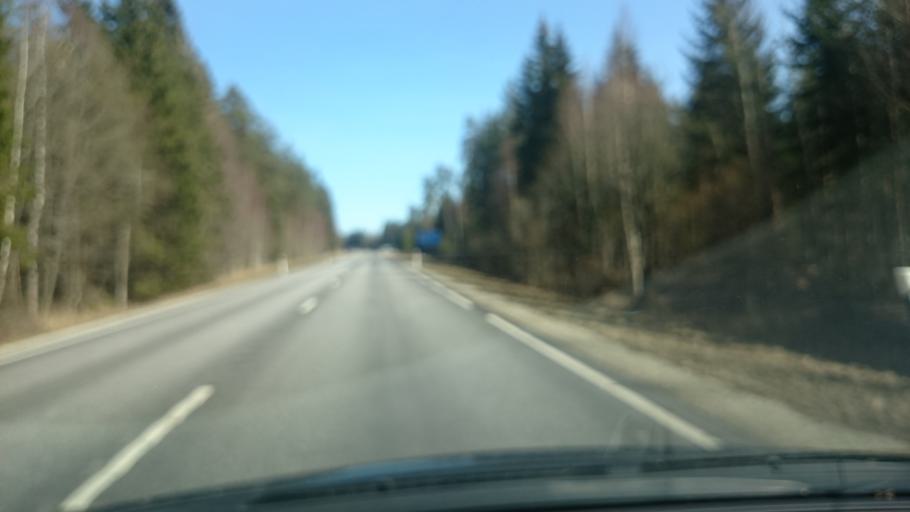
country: EE
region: Paernumaa
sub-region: Vaendra vald (alev)
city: Vandra
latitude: 58.6725
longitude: 25.2061
